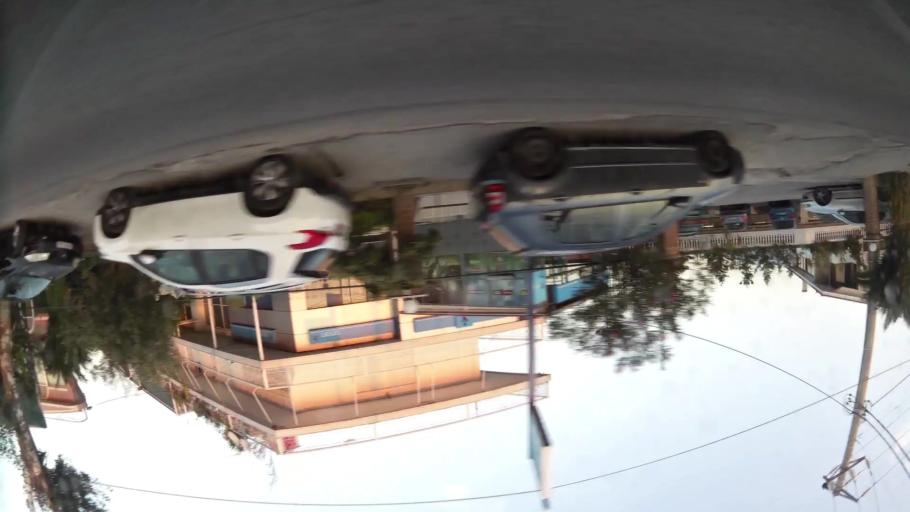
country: GR
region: Attica
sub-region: Nomarchia Anatolikis Attikis
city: Acharnes
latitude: 38.0928
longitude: 23.7544
